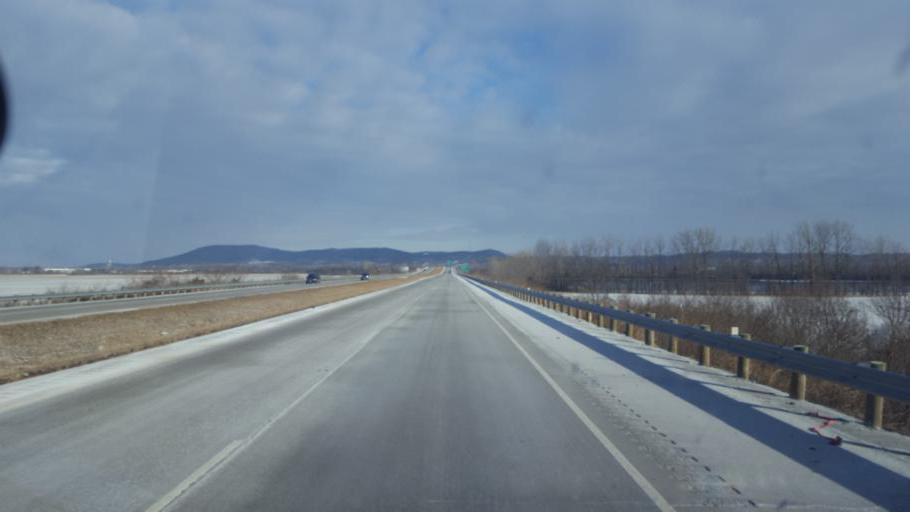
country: US
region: Ohio
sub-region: Ross County
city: Chillicothe
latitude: 39.3021
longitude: -82.9422
